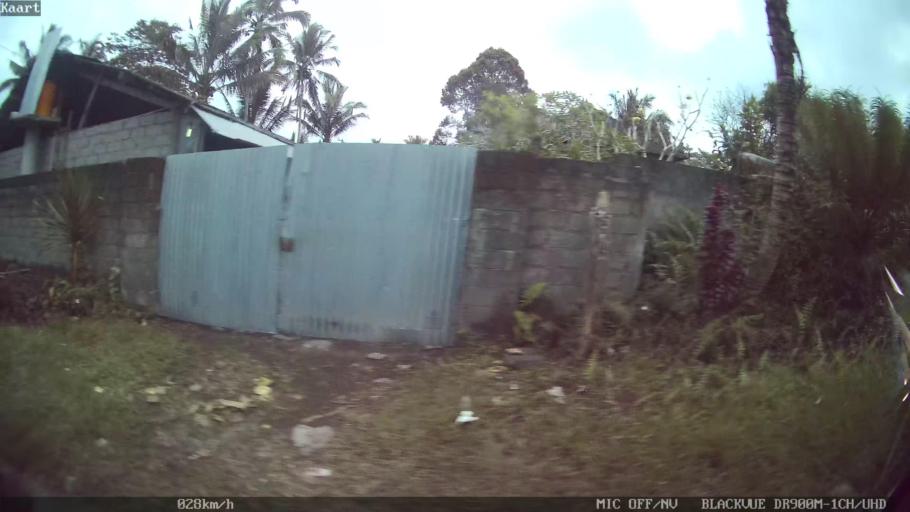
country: ID
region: Bali
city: Banjar Geriana Kangin
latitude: -8.4006
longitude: 115.4401
